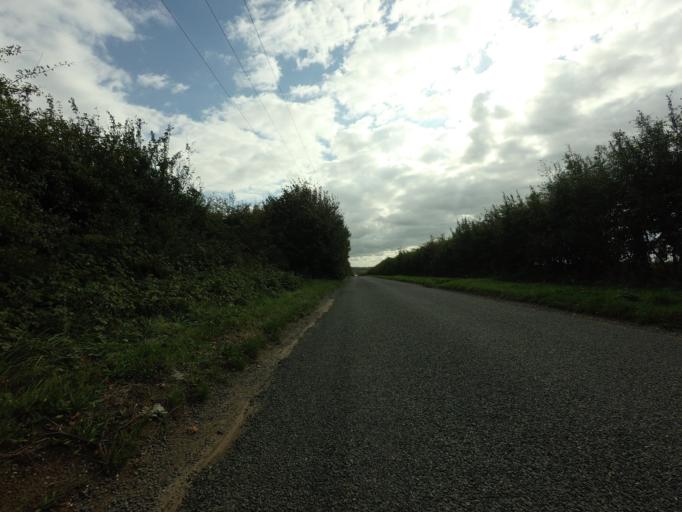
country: GB
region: England
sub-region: Norfolk
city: Heacham
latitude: 52.9171
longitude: 0.5425
